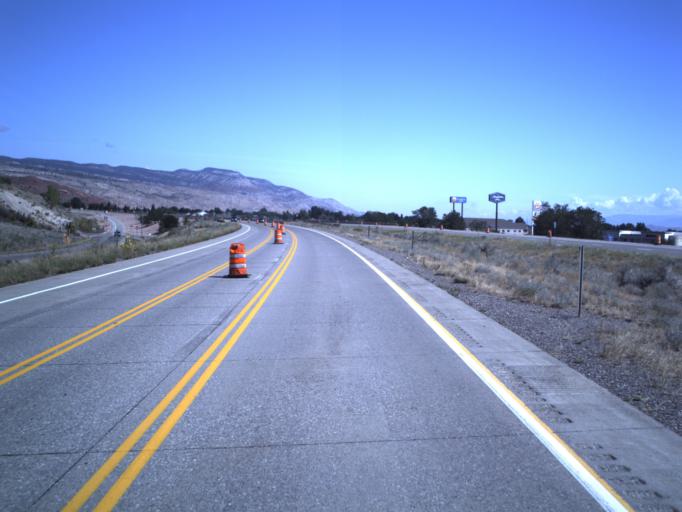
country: US
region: Utah
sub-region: Sevier County
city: Richfield
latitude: 38.7470
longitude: -112.1075
